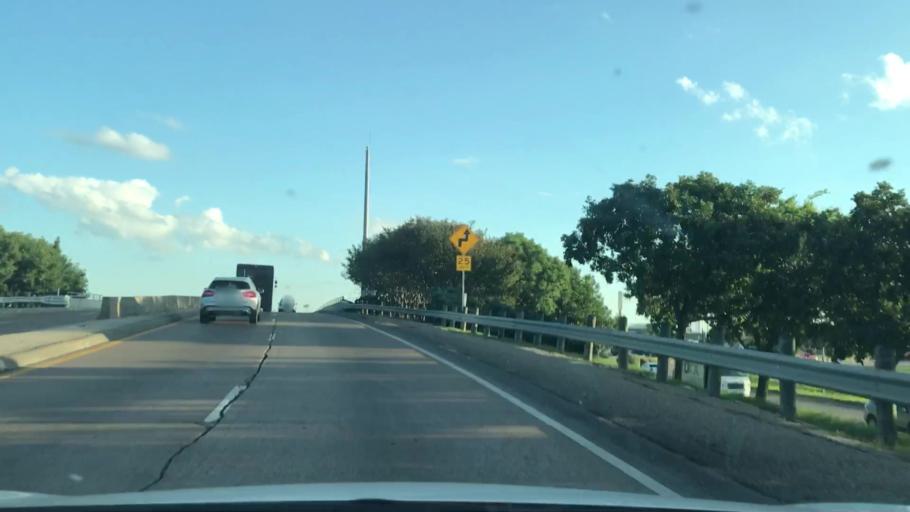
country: US
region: Texas
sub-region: Dallas County
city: Mesquite
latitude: 32.8047
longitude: -96.6685
